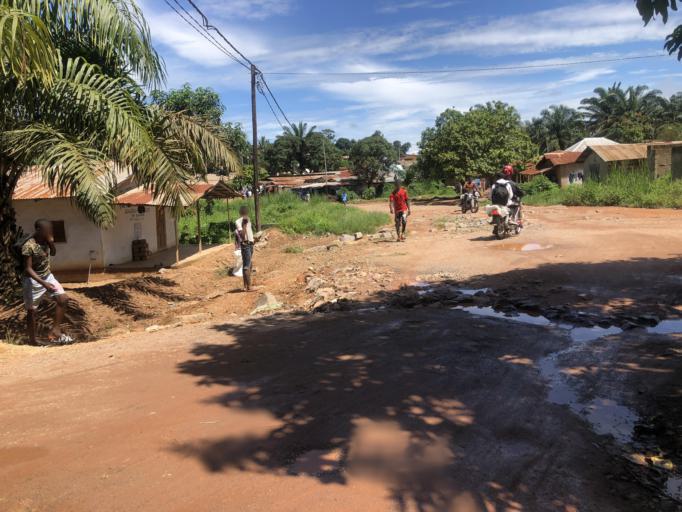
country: SL
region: Eastern Province
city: Koidu
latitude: 8.6452
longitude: -10.9548
